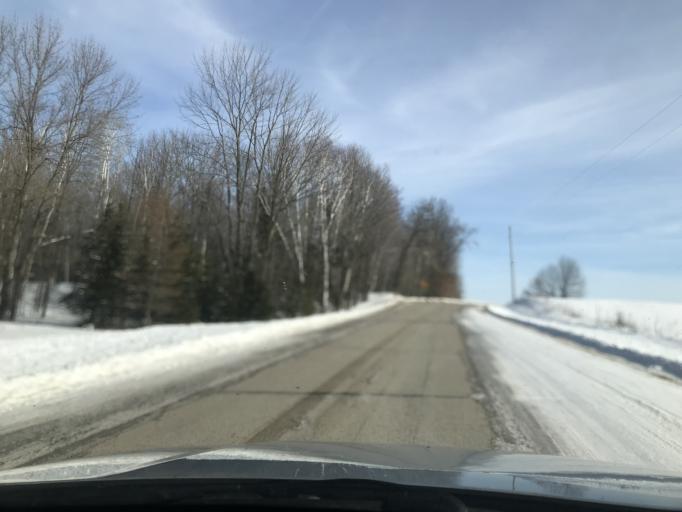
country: US
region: Wisconsin
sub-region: Oconto County
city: Gillett
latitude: 45.1201
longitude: -88.2416
